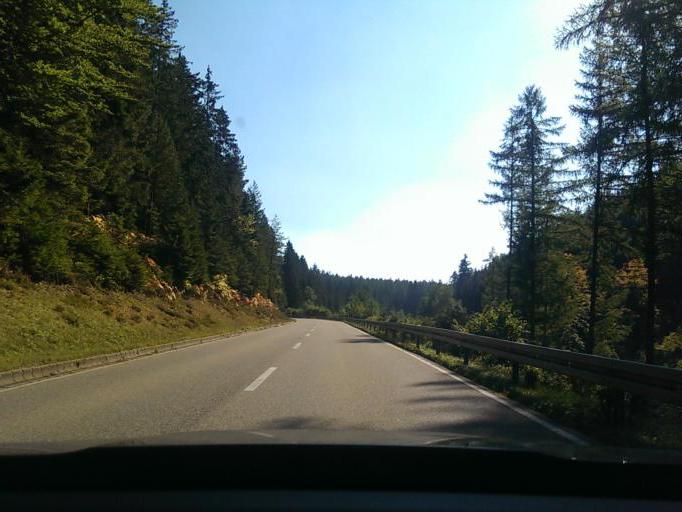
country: DE
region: Baden-Wuerttemberg
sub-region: Karlsruhe Region
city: Simmersfeld
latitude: 48.6516
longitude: 8.5159
